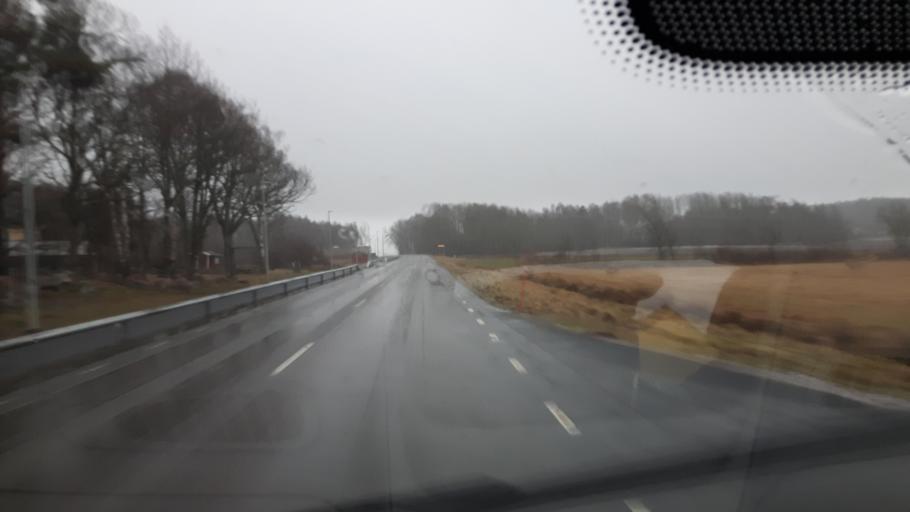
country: SE
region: Halland
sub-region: Kungsbacka Kommun
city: Vallda
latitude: 57.4193
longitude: 11.9453
